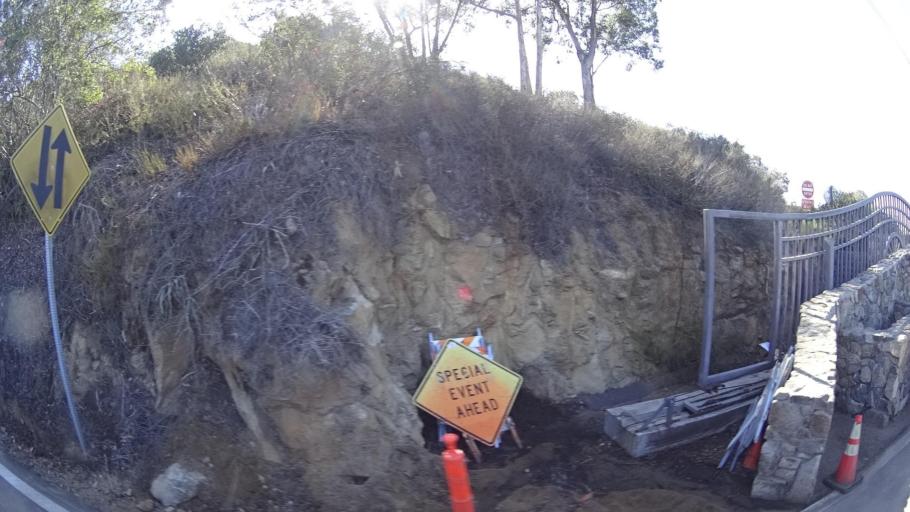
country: US
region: California
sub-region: San Diego County
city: Casa de Oro-Mount Helix
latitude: 32.7672
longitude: -116.9843
